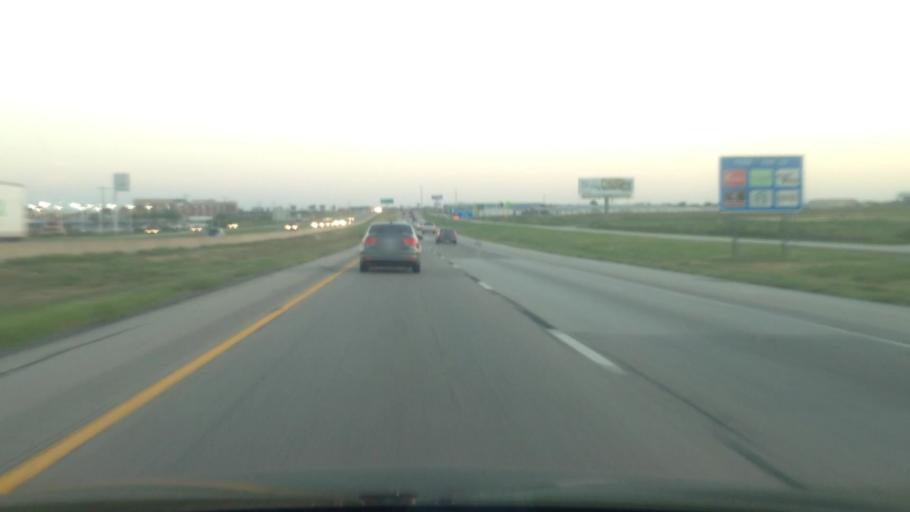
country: US
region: Texas
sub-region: Tarrant County
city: Haslet
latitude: 32.9393
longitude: -97.3134
